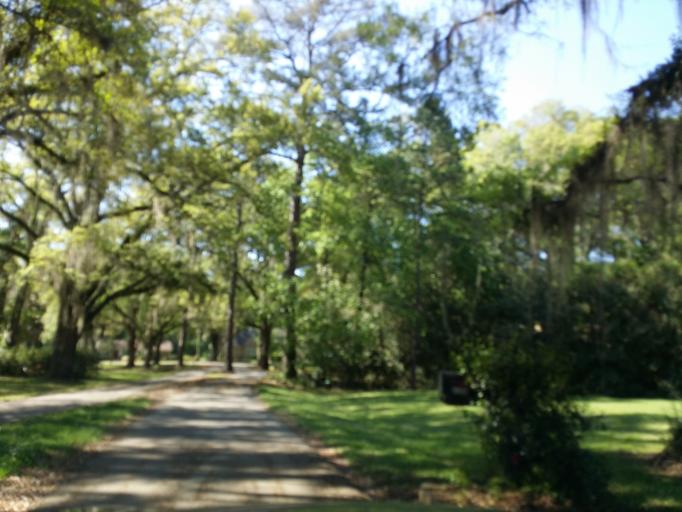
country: US
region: Florida
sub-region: Leon County
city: Tallahassee
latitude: 30.4855
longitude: -84.1865
